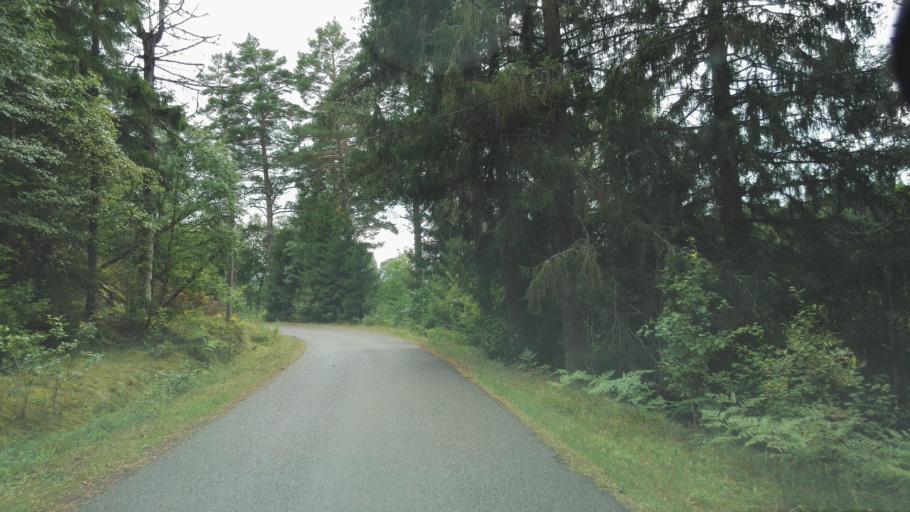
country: SE
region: Joenkoeping
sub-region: Vetlanda Kommun
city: Landsbro
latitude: 57.2145
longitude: 14.9524
